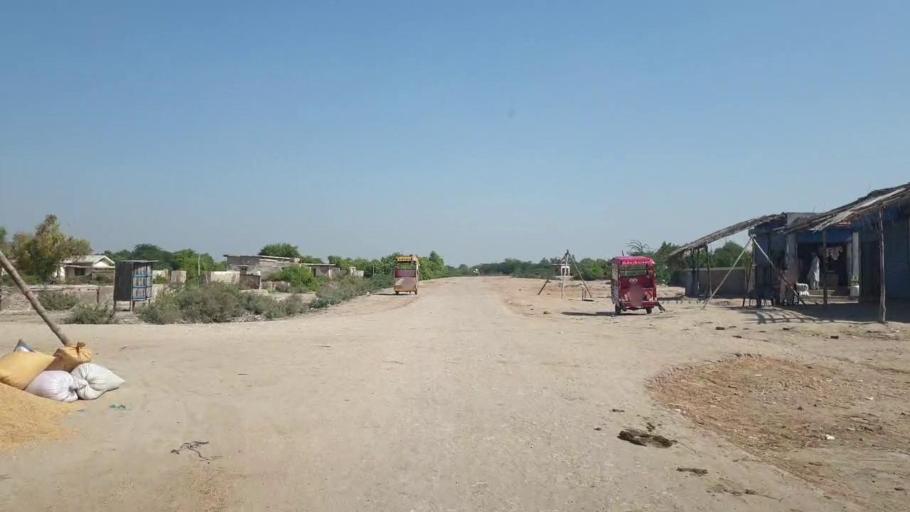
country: PK
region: Sindh
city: Talhar
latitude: 24.7908
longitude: 68.7972
